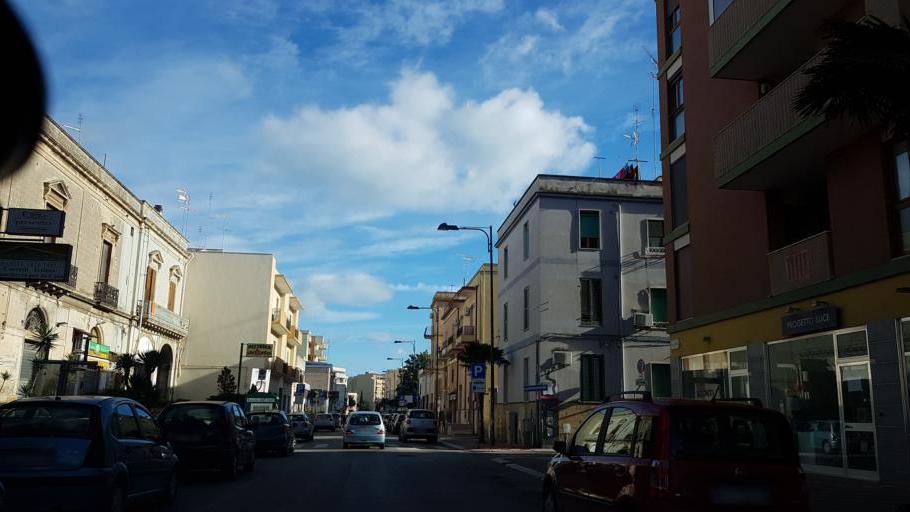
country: IT
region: Apulia
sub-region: Provincia di Brindisi
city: Brindisi
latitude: 40.6338
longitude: 17.9334
